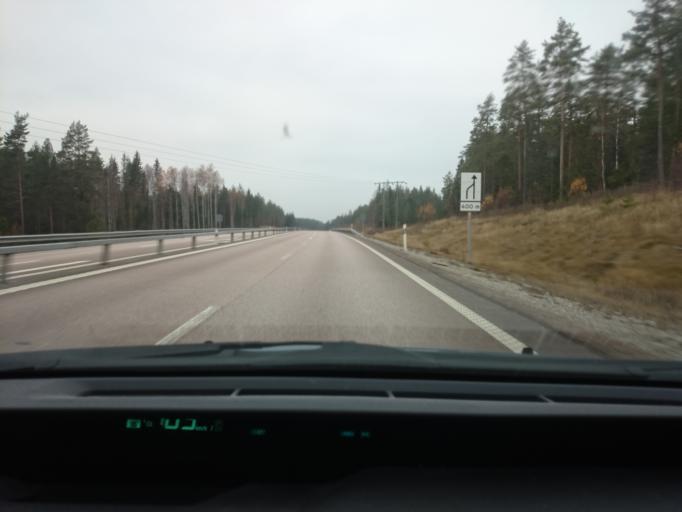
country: SE
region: Vaestmanland
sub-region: Sala Kommun
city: Sala
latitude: 60.0101
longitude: 16.3918
